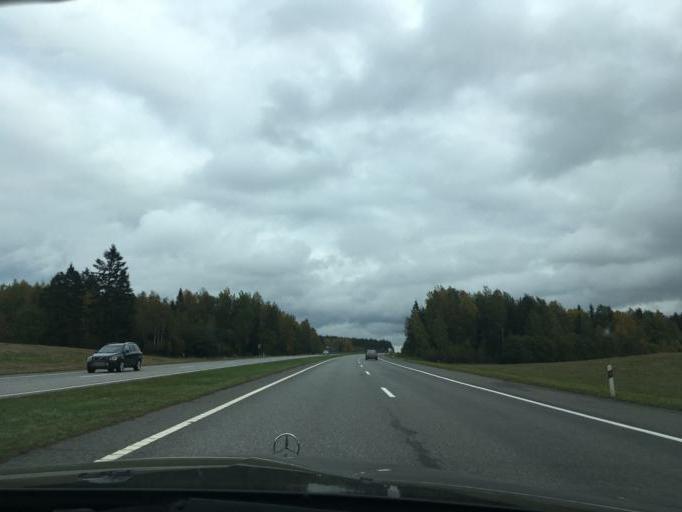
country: BY
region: Vitebsk
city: Talachyn
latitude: 54.4791
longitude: 29.8392
